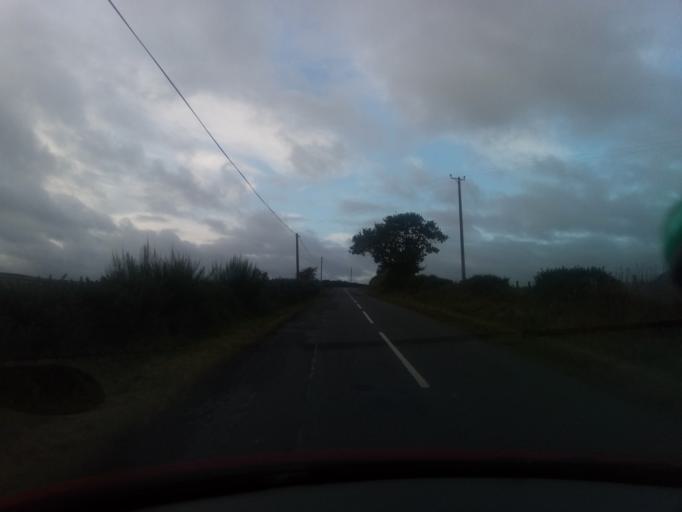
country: GB
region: Scotland
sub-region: The Scottish Borders
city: Jedburgh
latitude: 55.4464
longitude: -2.5741
